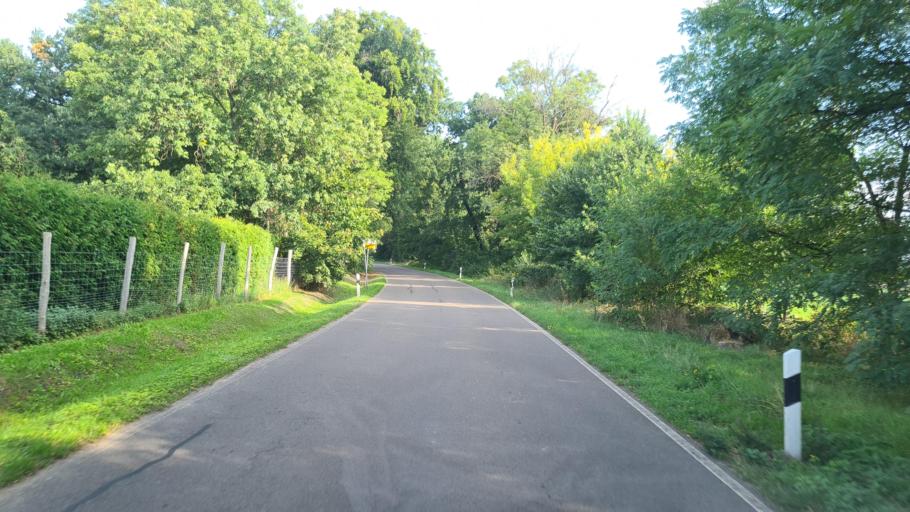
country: DE
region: Brandenburg
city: Neupetershain
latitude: 51.6531
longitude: 14.1765
